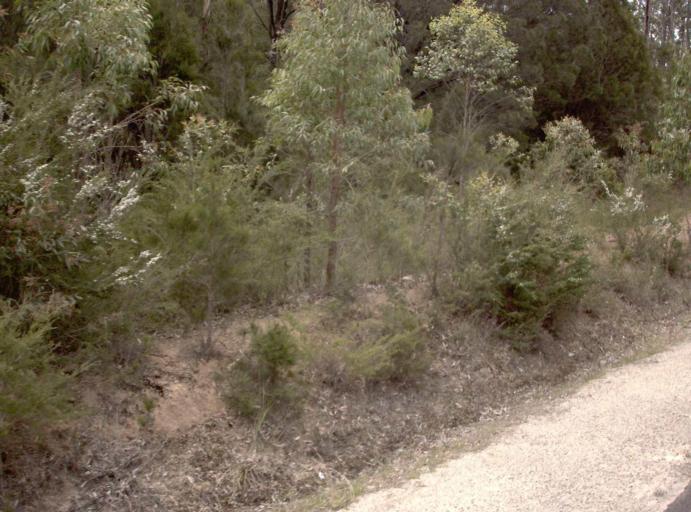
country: AU
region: New South Wales
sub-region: Bega Valley
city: Eden
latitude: -37.4543
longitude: 149.6170
